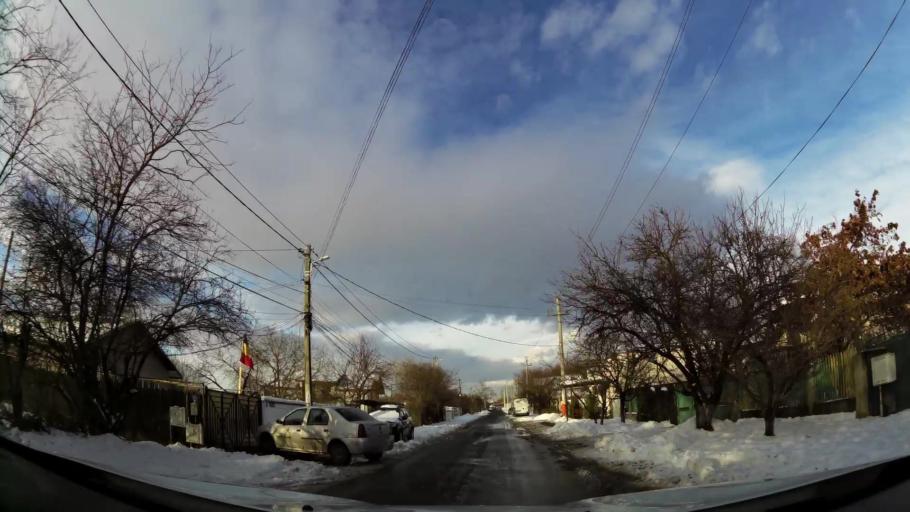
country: RO
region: Ilfov
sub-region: Comuna Jilava
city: Jilava
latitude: 44.3395
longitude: 26.0836
